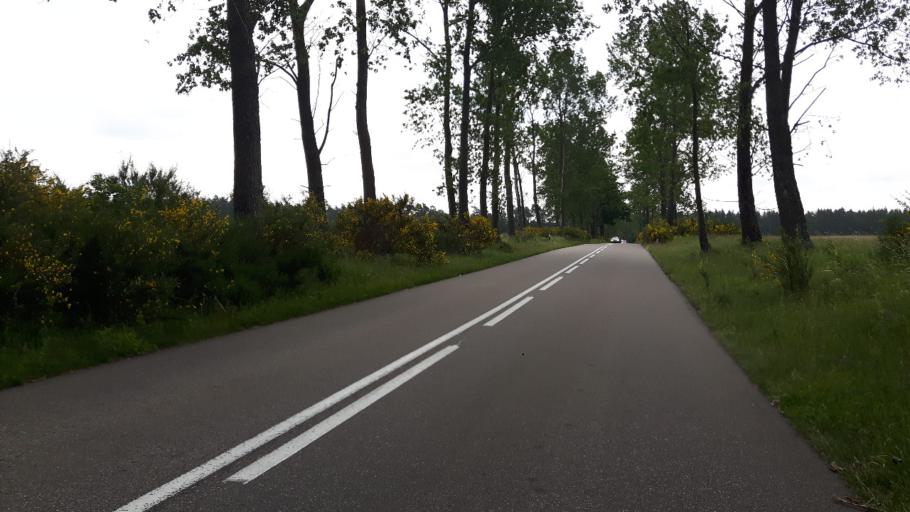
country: PL
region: Pomeranian Voivodeship
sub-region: Powiat leborski
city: Leba
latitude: 54.7477
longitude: 17.7116
